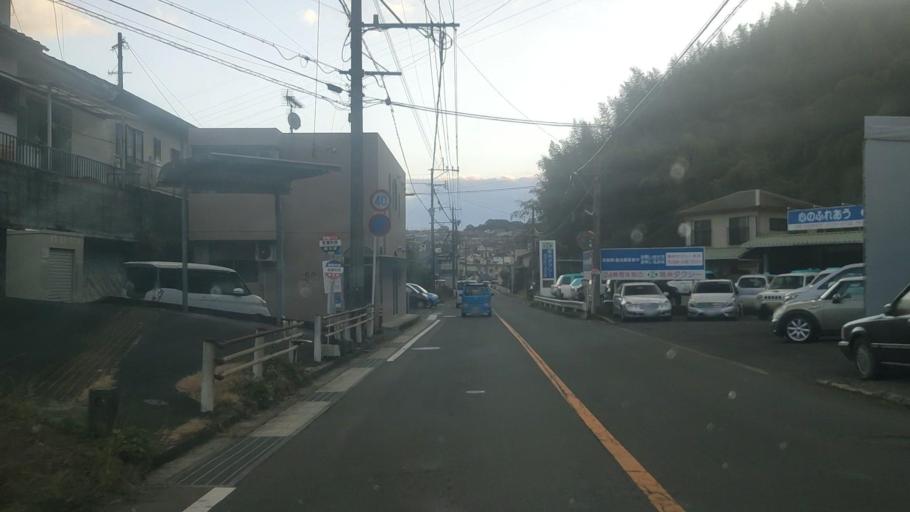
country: JP
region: Kagoshima
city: Kagoshima-shi
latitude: 31.6253
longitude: 130.5431
